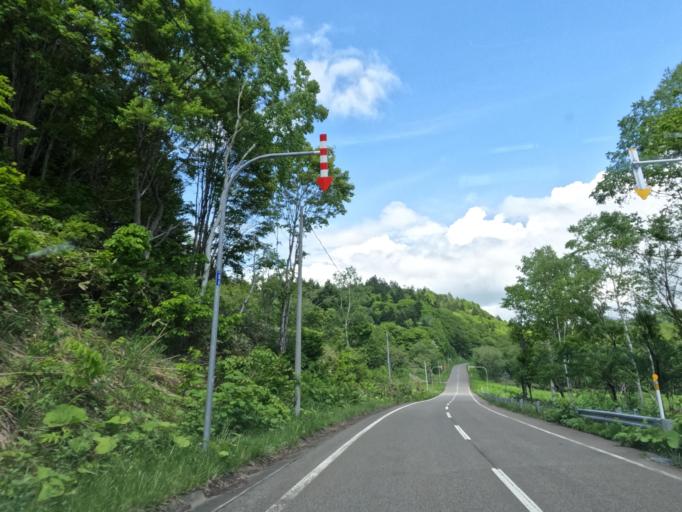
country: JP
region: Hokkaido
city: Takikawa
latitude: 43.5377
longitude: 141.6006
